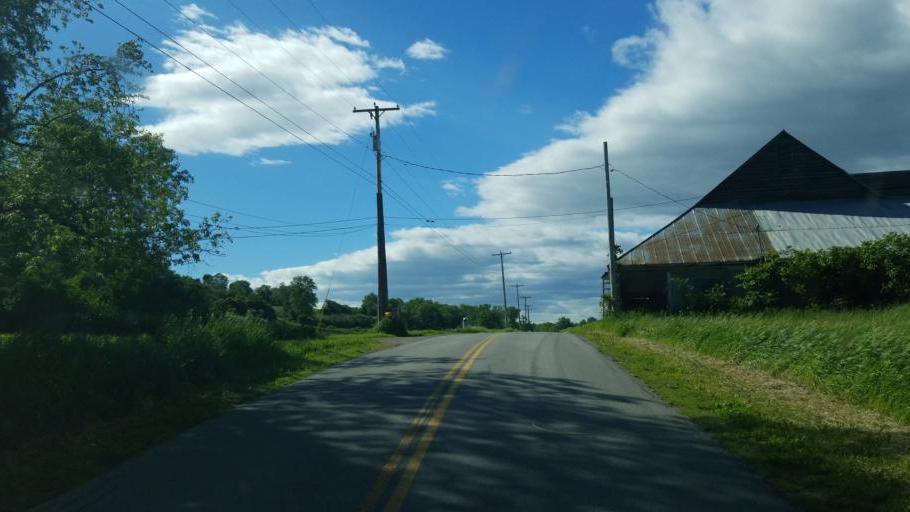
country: US
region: New York
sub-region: Montgomery County
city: Fort Plain
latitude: 42.9662
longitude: -74.6453
